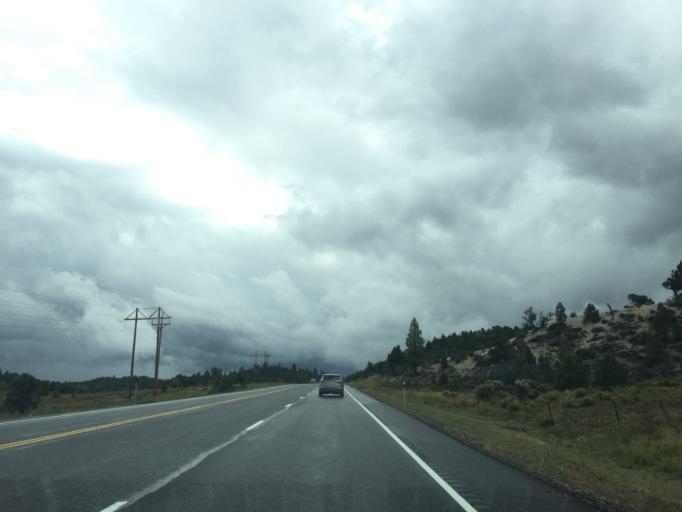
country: US
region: Utah
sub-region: Garfield County
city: Panguitch
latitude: 37.5056
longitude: -112.4991
